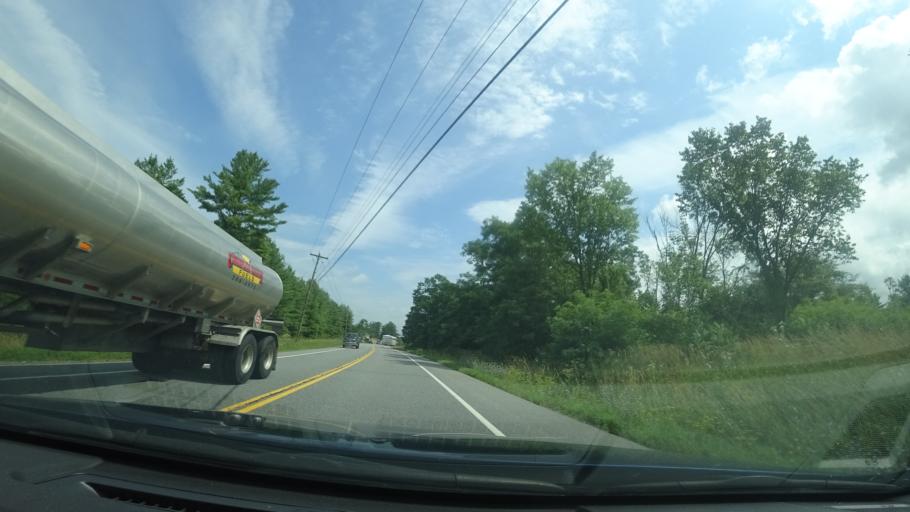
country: US
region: New York
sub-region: Warren County
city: Queensbury
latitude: 43.3732
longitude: -73.5162
